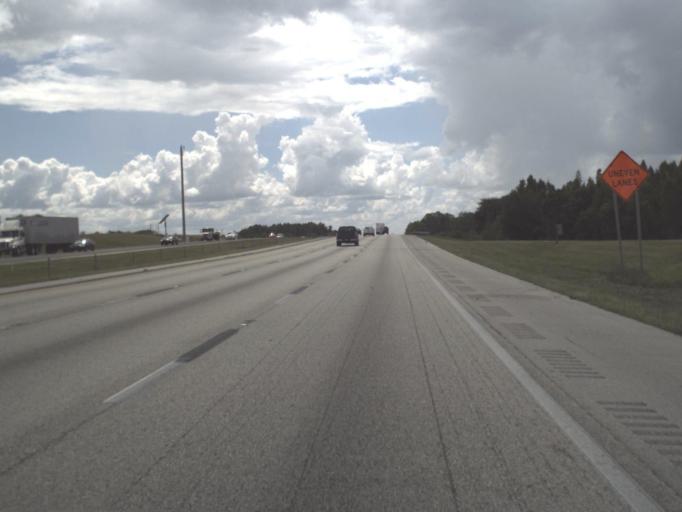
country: US
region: Florida
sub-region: Polk County
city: Davenport
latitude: 28.2046
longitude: -81.6922
